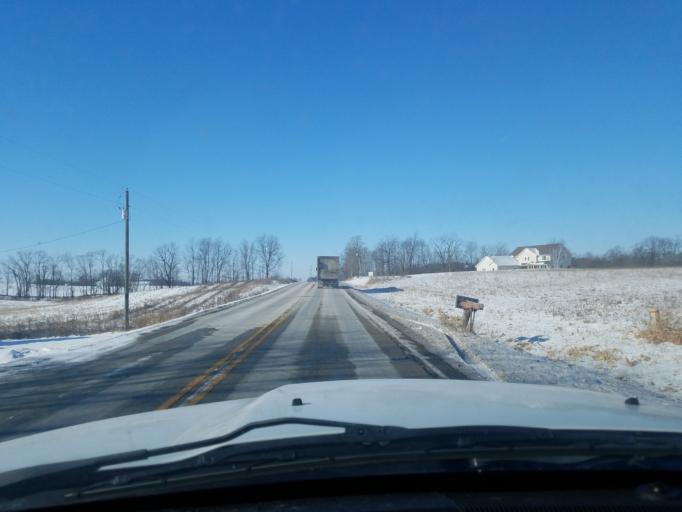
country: US
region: Indiana
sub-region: Noble County
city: Avilla
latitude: 41.3946
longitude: -85.2625
